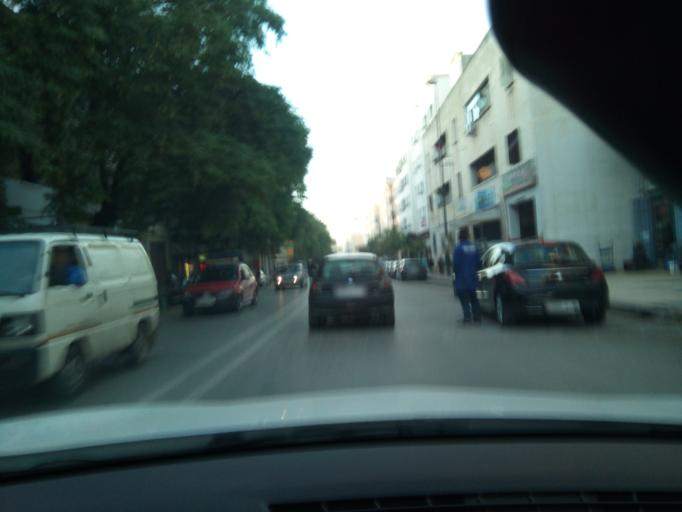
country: MA
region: Fes-Boulemane
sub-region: Fes
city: Fes
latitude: 34.0297
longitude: -4.9928
